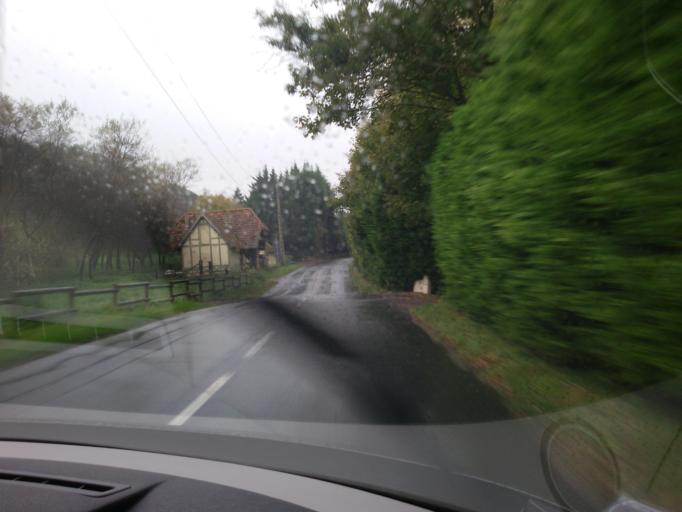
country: FR
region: Lower Normandy
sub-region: Departement du Calvados
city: Trouville-sur-Mer
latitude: 49.3929
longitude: 0.1181
